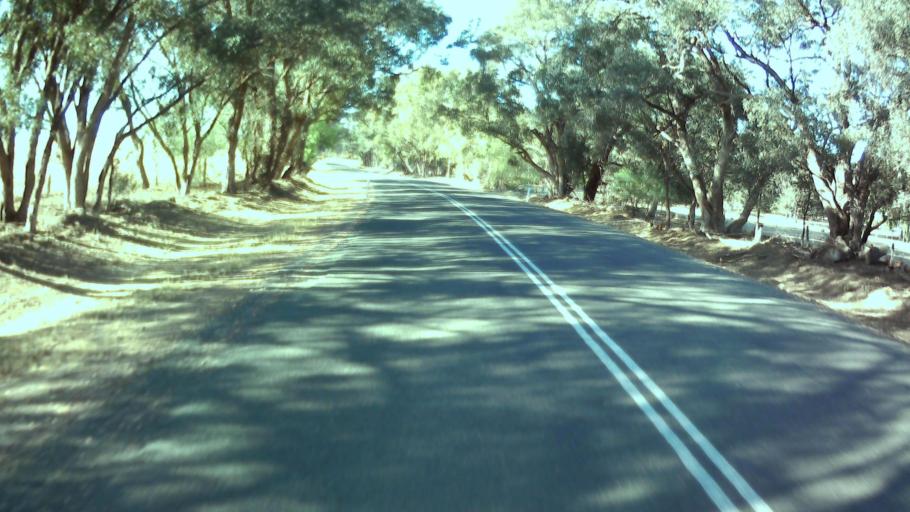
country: AU
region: New South Wales
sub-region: Weddin
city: Grenfell
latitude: -33.9952
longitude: 148.1325
